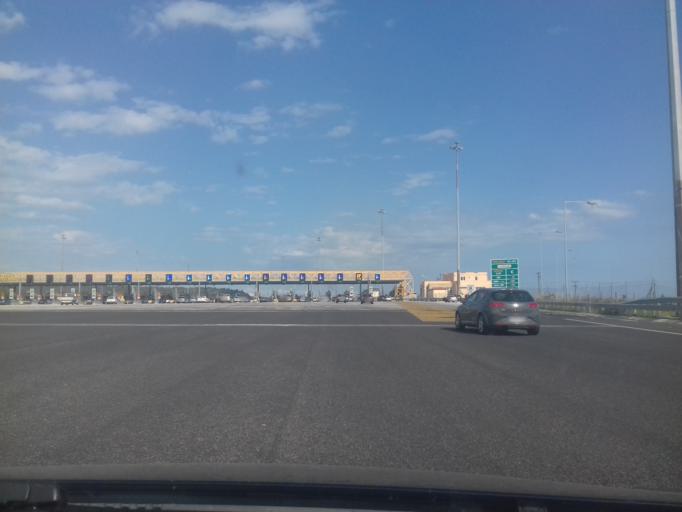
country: GR
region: Peloponnese
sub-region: Nomos Korinthias
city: Isthmia
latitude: 37.9249
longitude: 23.0300
